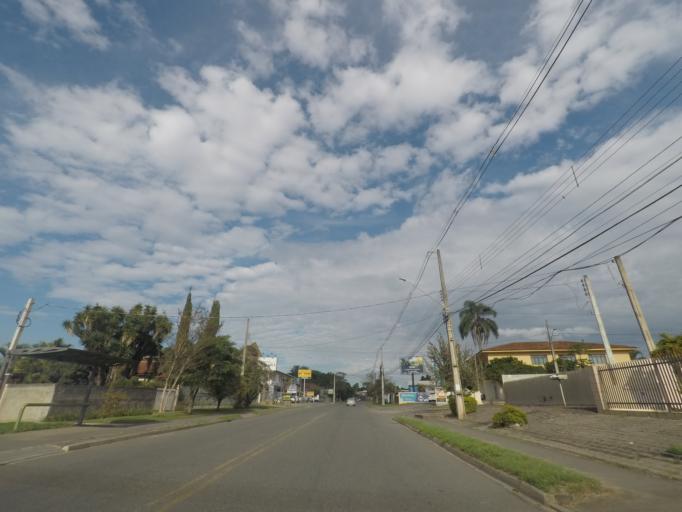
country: BR
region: Parana
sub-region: Sao Jose Dos Pinhais
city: Sao Jose dos Pinhais
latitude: -25.5657
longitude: -49.2884
